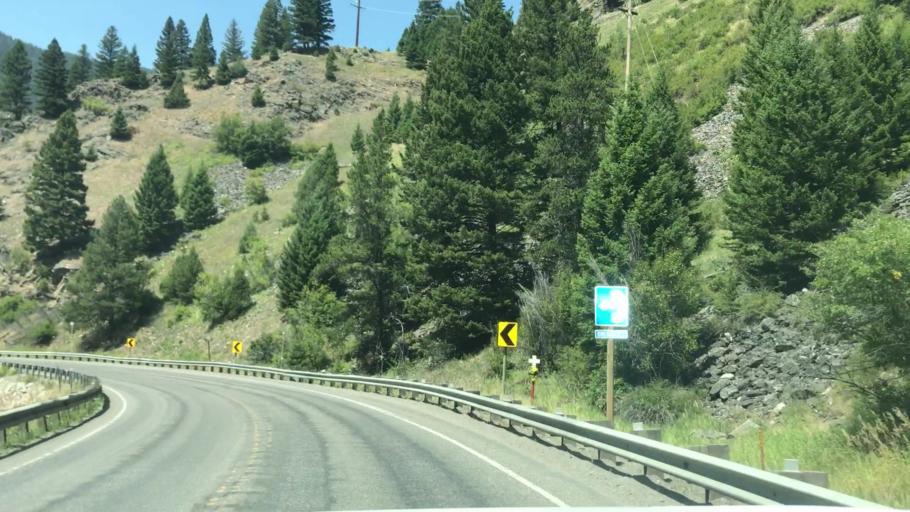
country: US
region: Montana
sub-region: Gallatin County
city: Big Sky
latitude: 45.4072
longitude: -111.2214
